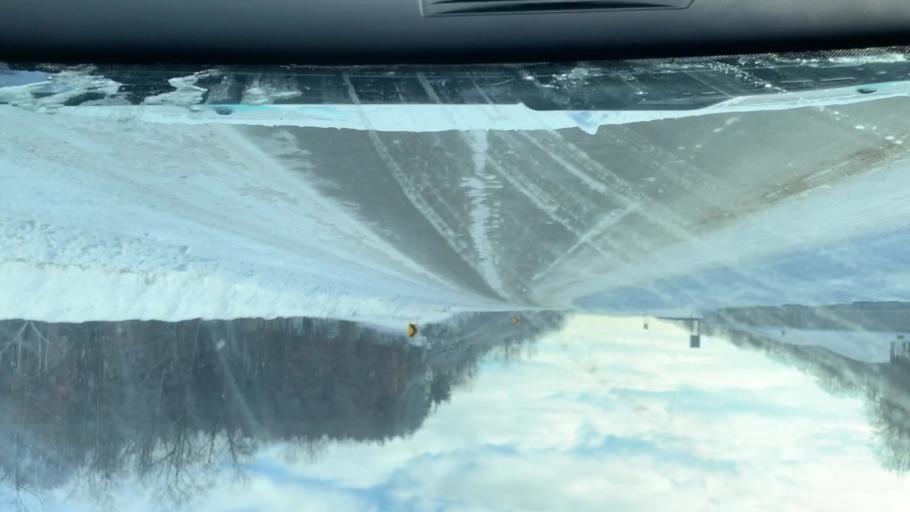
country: US
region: Michigan
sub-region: Wexford County
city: Cadillac
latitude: 44.2997
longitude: -85.3924
